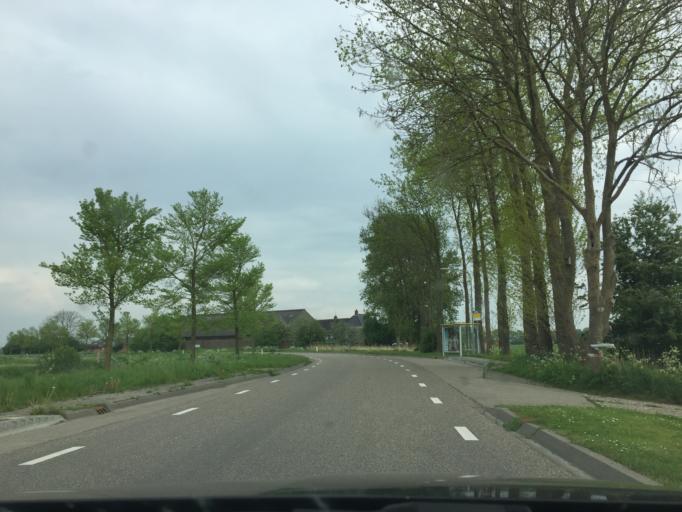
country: NL
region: Groningen
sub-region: Gemeente Zuidhorn
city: Aduard
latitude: 53.2664
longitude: 6.4400
